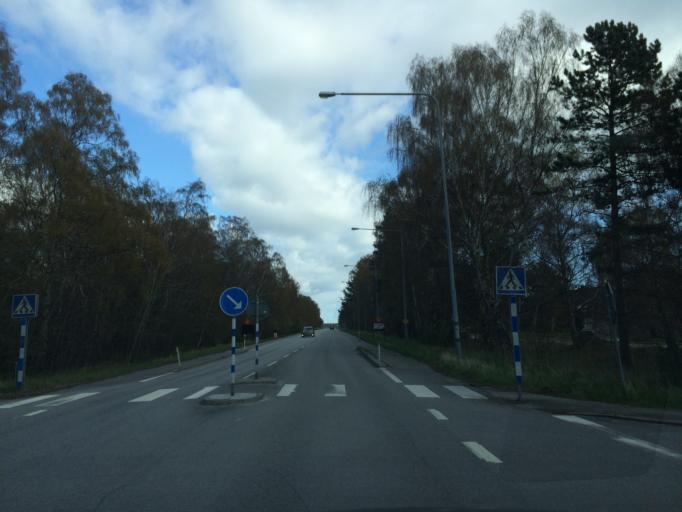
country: SE
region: Skane
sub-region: Vellinge Kommun
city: Skanor med Falsterbo
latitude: 55.4068
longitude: 12.8553
